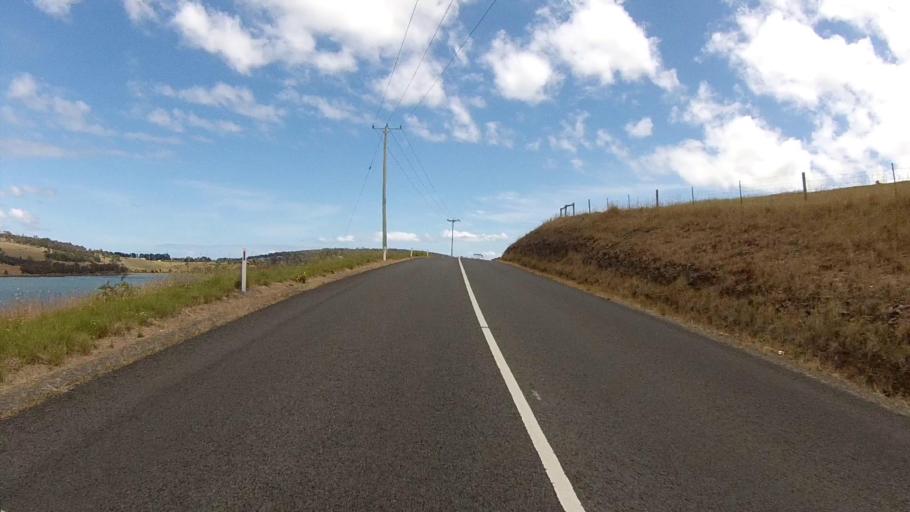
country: AU
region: Tasmania
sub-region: Sorell
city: Sorell
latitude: -42.8687
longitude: 147.6724
